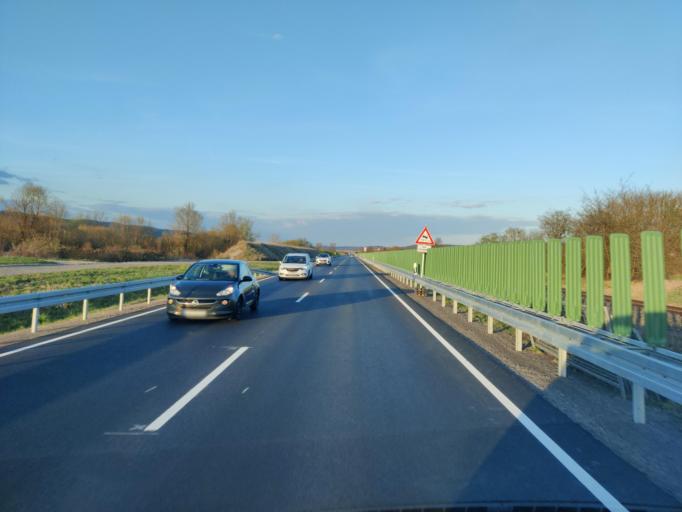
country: DE
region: Baden-Wuerttemberg
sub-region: Tuebingen Region
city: Rottenburg
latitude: 48.4830
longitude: 8.9845
